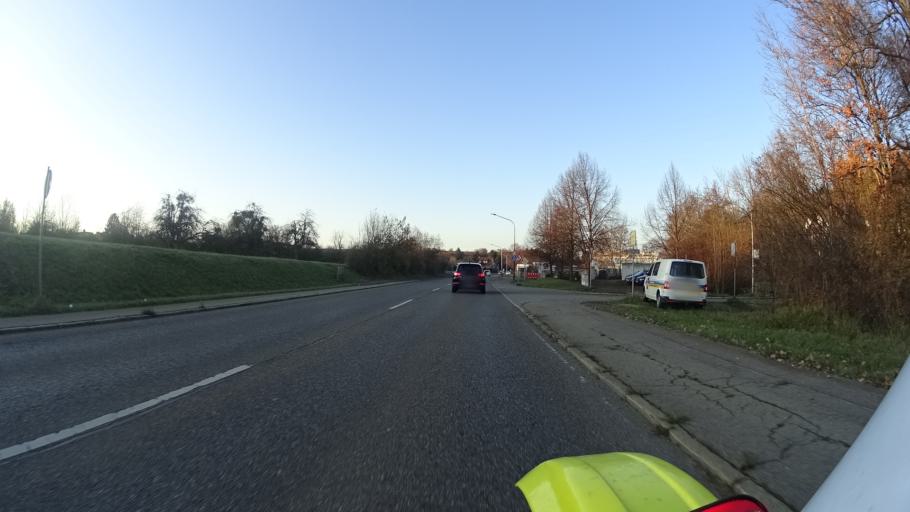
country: DE
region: Baden-Wuerttemberg
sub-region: Regierungsbezirk Stuttgart
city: Schlat
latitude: 48.6735
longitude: 9.6894
